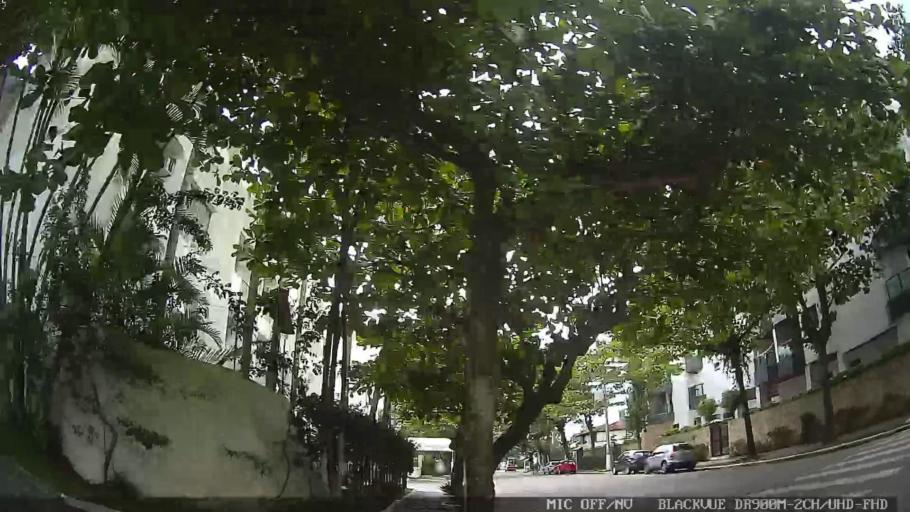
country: BR
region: Sao Paulo
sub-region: Guaruja
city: Guaruja
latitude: -23.9882
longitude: -46.2432
